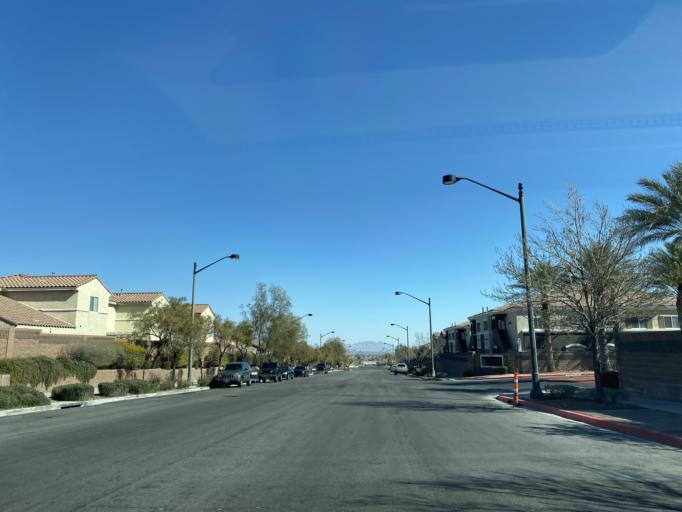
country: US
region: Nevada
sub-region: Clark County
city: Summerlin South
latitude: 36.3029
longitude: -115.2999
